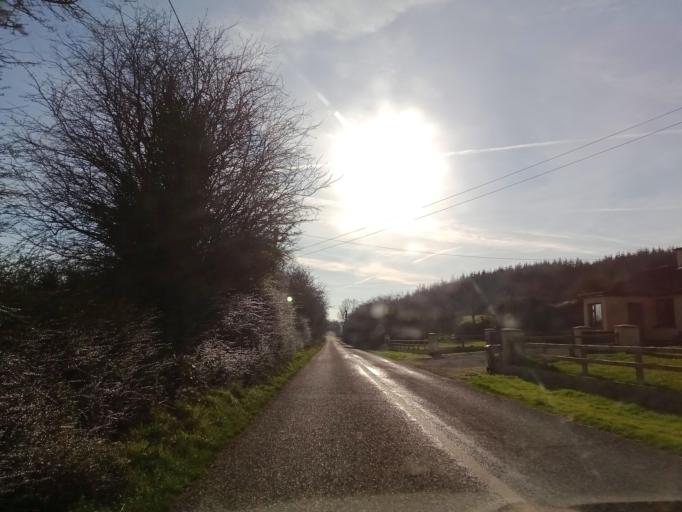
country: IE
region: Munster
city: Fethard
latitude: 52.5774
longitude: -7.5663
